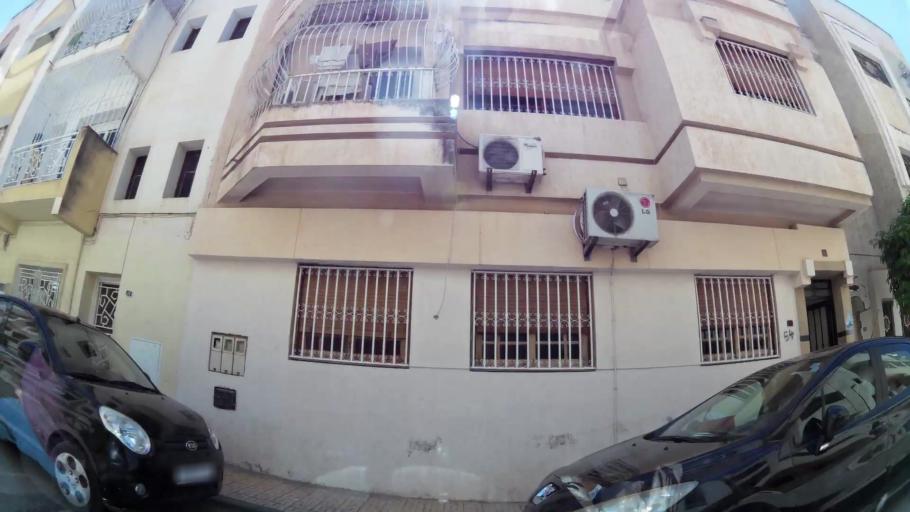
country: MA
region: Fes-Boulemane
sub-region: Fes
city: Fes
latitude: 34.0264
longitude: -5.0108
